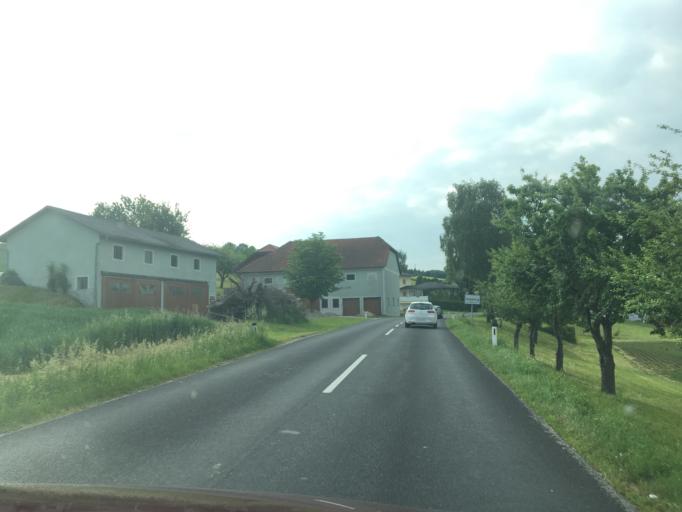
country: AT
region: Upper Austria
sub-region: Politischer Bezirk Grieskirchen
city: Grieskirchen
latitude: 48.3172
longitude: 13.8338
